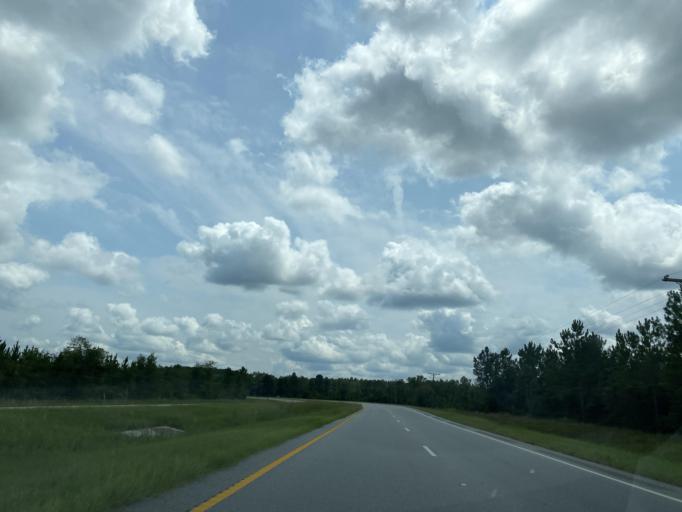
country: US
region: Georgia
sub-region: Ware County
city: Deenwood
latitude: 31.2806
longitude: -82.4513
